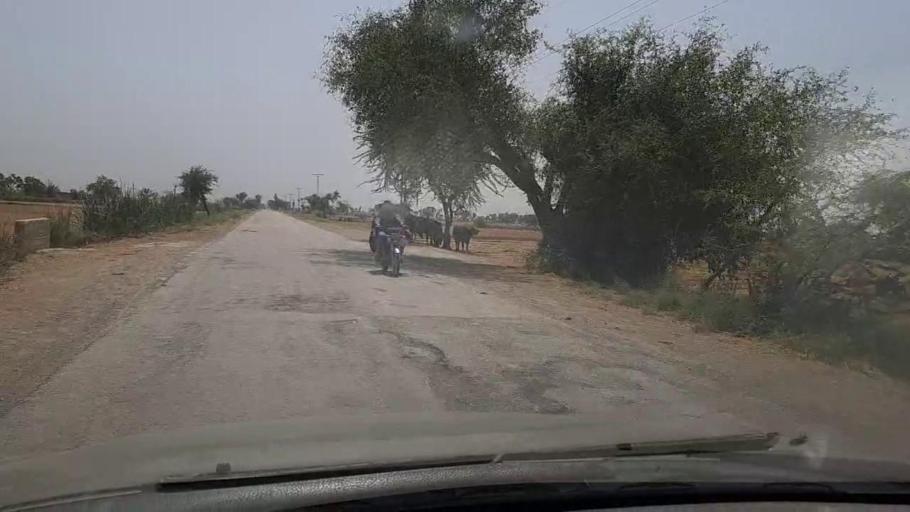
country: PK
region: Sindh
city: Miro Khan
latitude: 27.7133
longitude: 68.0659
